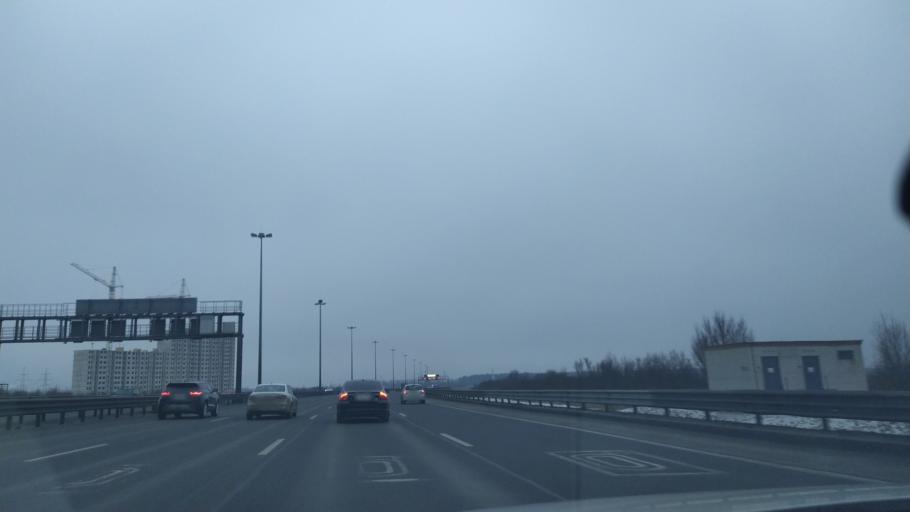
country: RU
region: St.-Petersburg
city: Krasnogvargeisky
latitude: 60.0073
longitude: 30.4760
